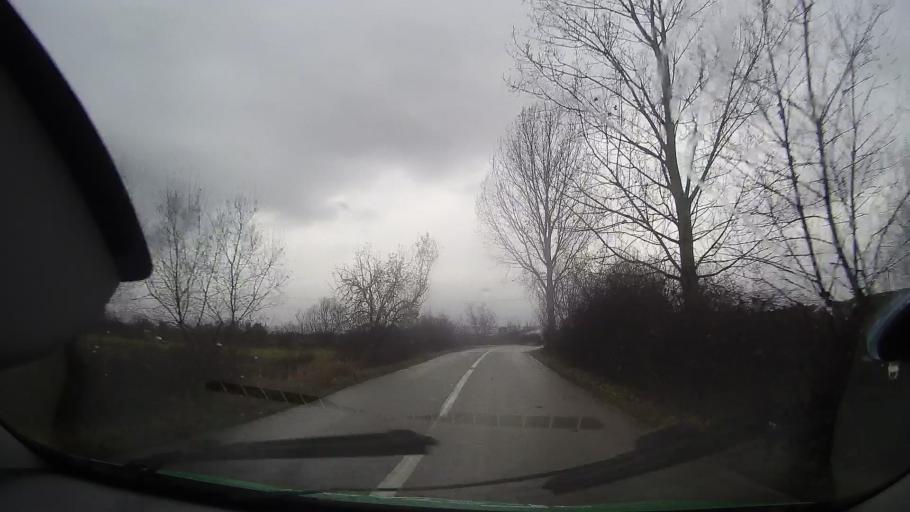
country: RO
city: Capalna
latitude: 46.7214
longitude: 22.0857
